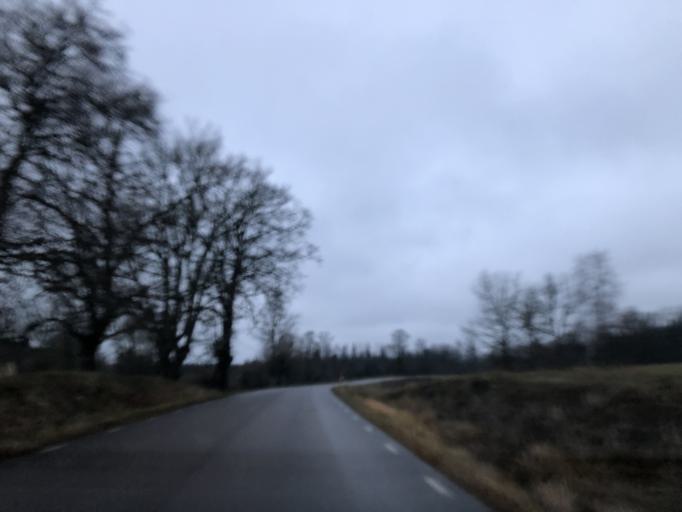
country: SE
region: Vaestra Goetaland
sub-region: Ulricehamns Kommun
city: Ulricehamn
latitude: 57.8457
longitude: 13.2654
